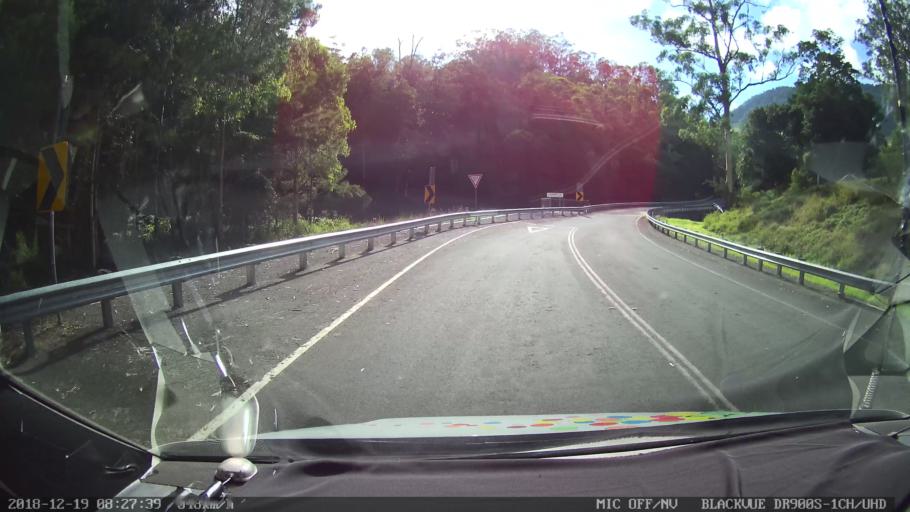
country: AU
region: New South Wales
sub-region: Kyogle
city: Kyogle
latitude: -28.3187
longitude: 152.9283
